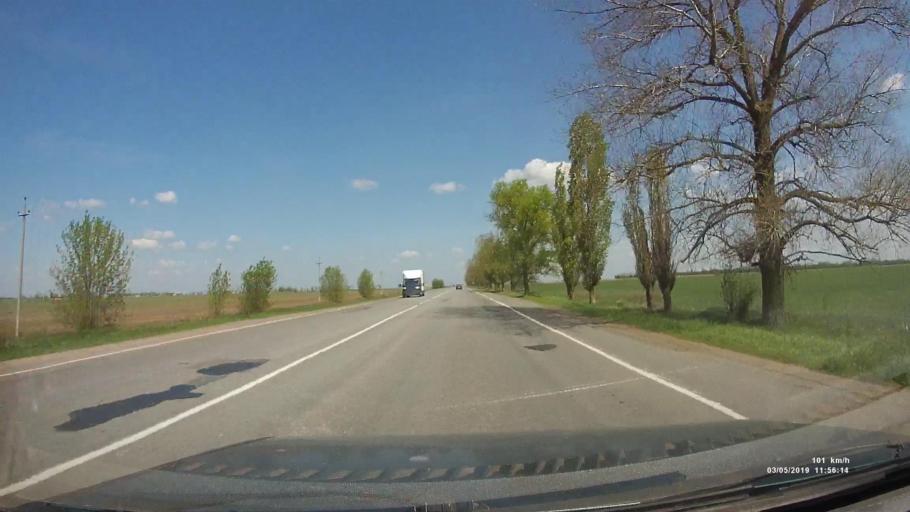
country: RU
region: Rostov
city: Bagayevskaya
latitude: 47.1919
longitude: 40.2990
